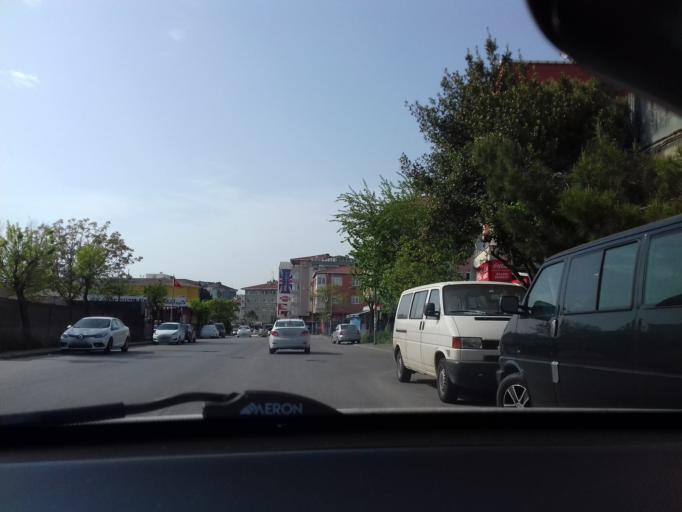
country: TR
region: Istanbul
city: Maltepe
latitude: 40.9144
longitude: 29.2082
